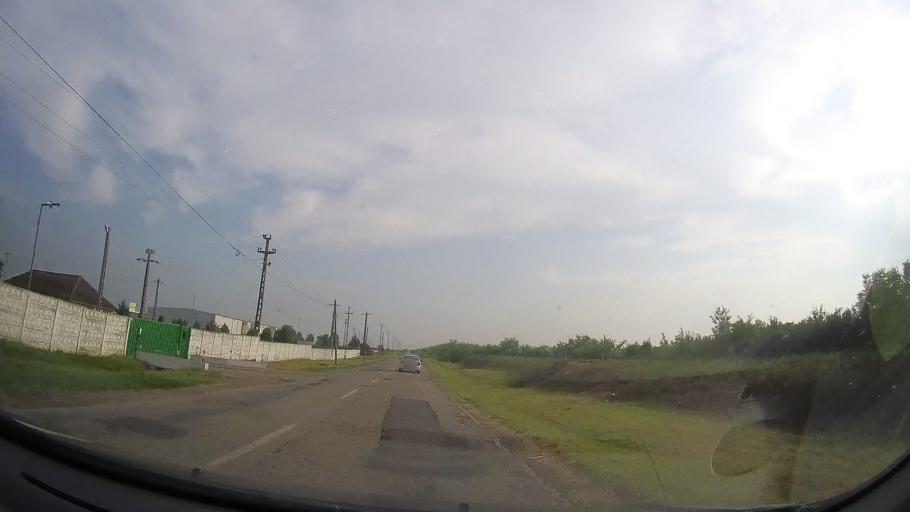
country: RO
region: Timis
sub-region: Comuna Giulvaz
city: Giulvaz
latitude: 45.5557
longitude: 20.9951
